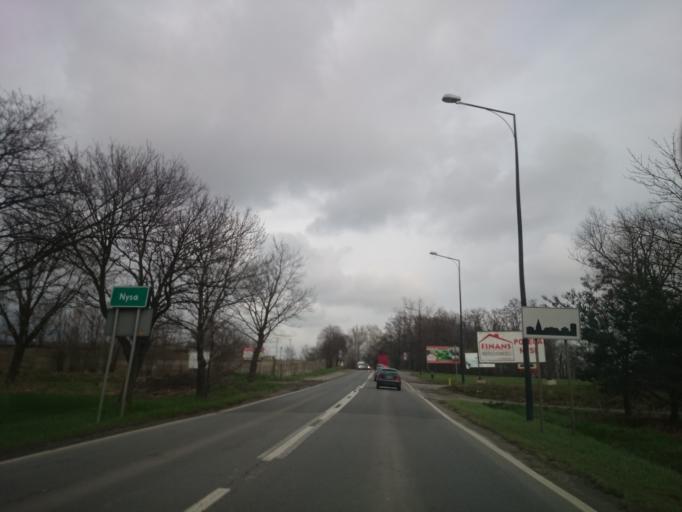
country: PL
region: Opole Voivodeship
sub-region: Powiat nyski
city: Nysa
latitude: 50.4789
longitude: 17.2928
